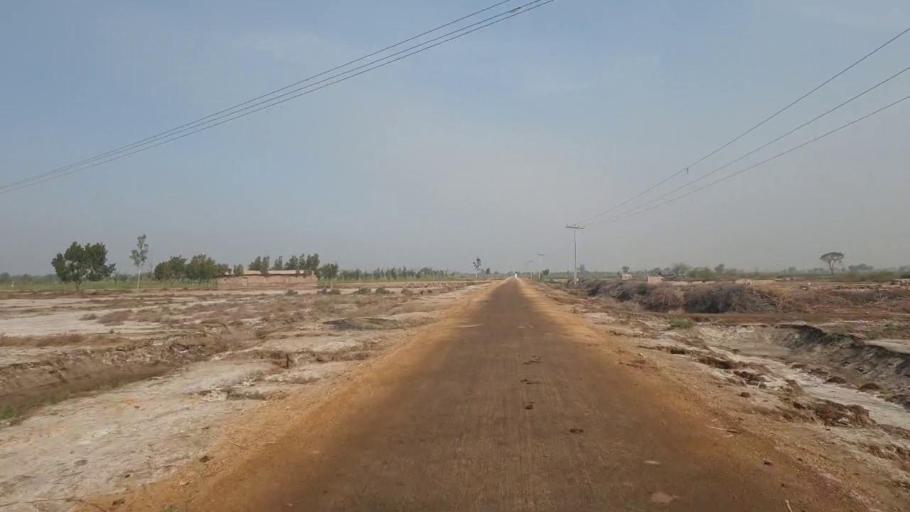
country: PK
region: Sindh
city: Mirwah Gorchani
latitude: 25.3683
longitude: 69.1665
